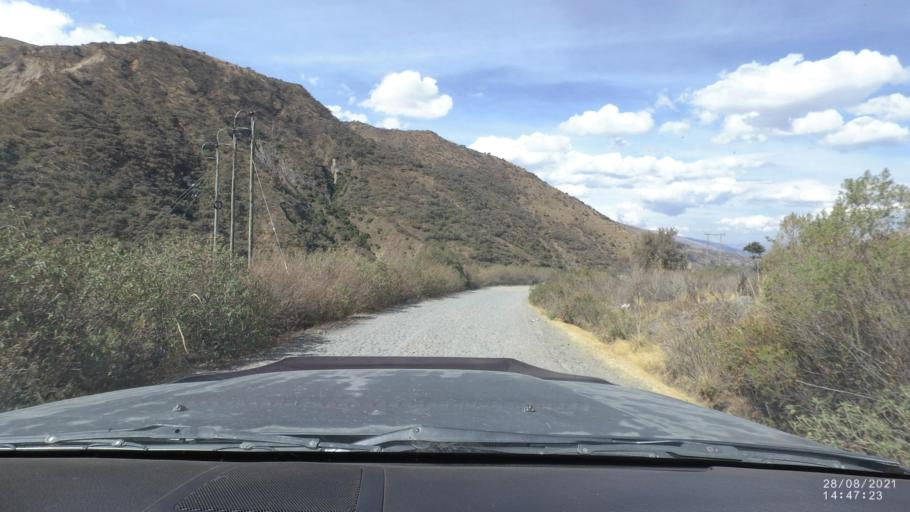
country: BO
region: Cochabamba
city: Sipe Sipe
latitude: -17.2772
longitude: -66.3219
